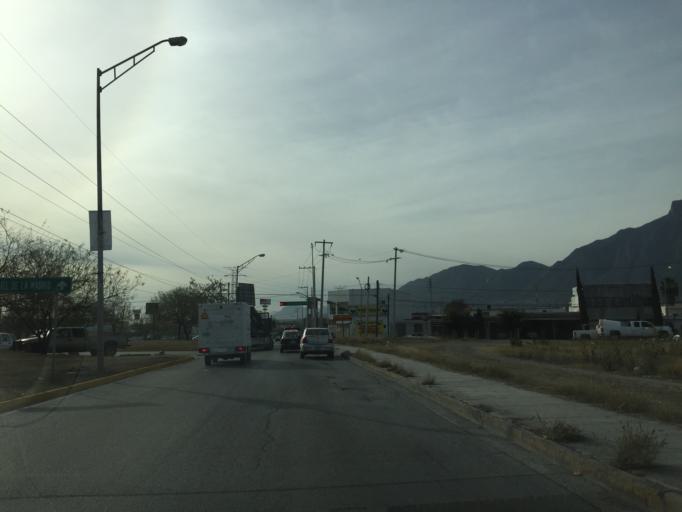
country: MX
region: Nuevo Leon
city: Guadalupe
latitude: 25.6975
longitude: -100.2132
